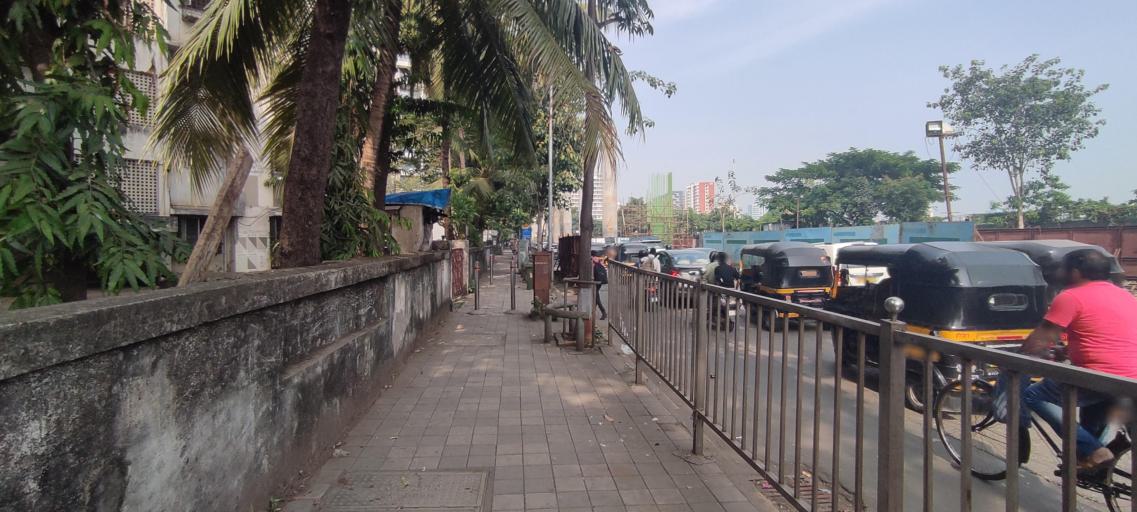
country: IN
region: Maharashtra
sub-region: Mumbai Suburban
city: Mumbai
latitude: 19.1180
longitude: 72.8297
